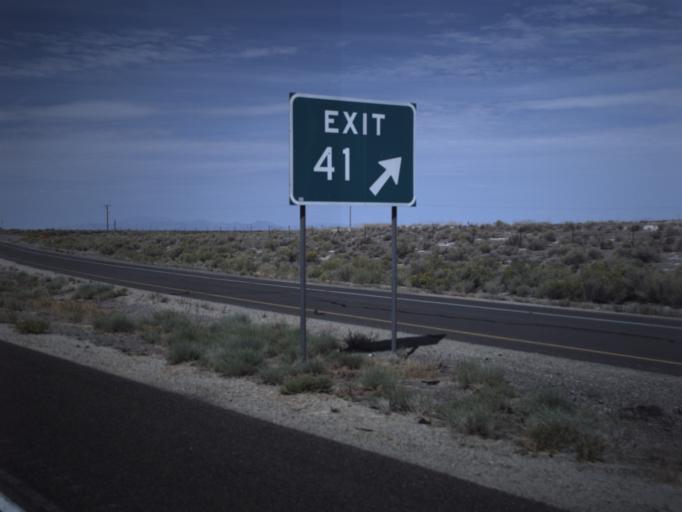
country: US
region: Utah
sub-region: Tooele County
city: Wendover
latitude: 40.7273
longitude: -113.2550
